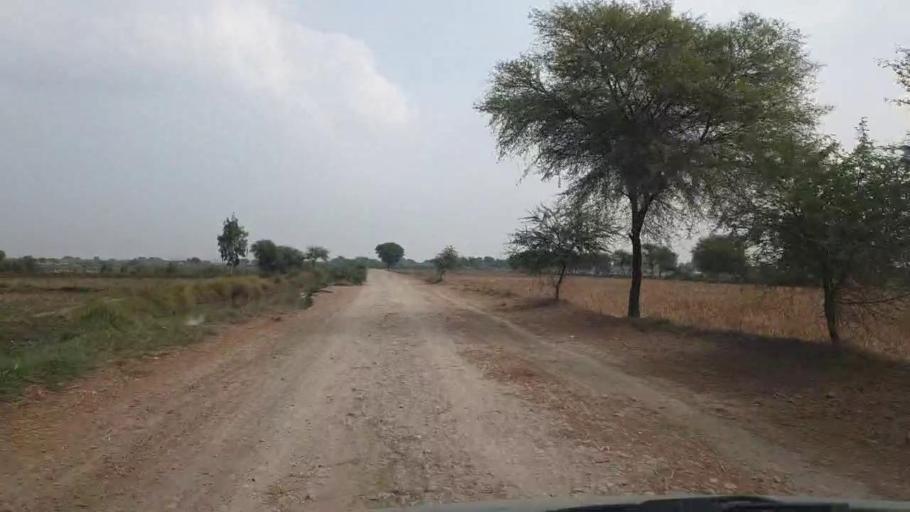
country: PK
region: Sindh
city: Matli
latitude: 24.9564
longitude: 68.7020
